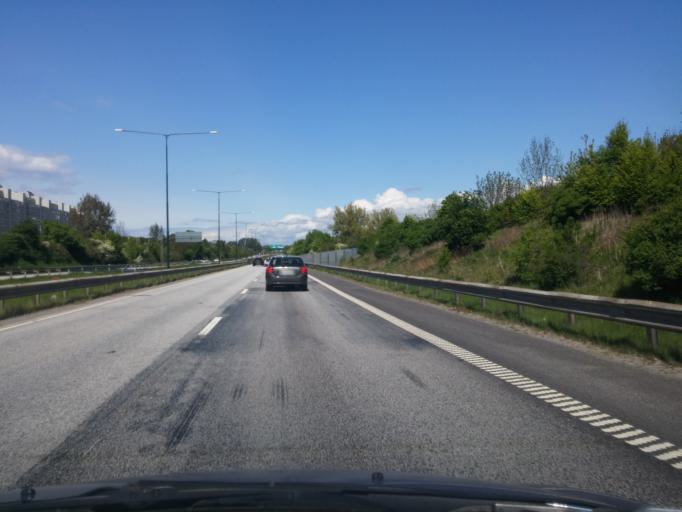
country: SE
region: Skane
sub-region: Burlovs Kommun
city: Arloev
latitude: 55.5878
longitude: 13.0561
